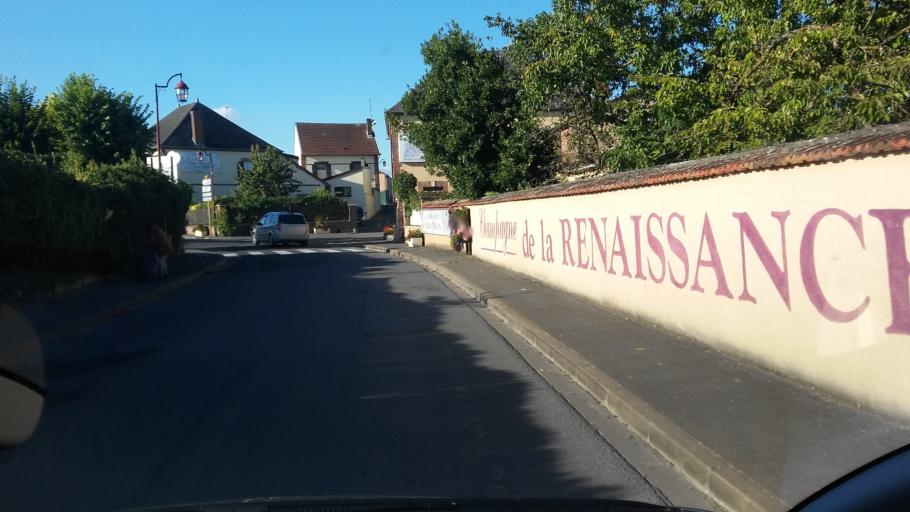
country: FR
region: Champagne-Ardenne
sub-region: Departement de la Marne
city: Le Mesnil-sur-Oger
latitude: 48.9588
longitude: 4.0138
